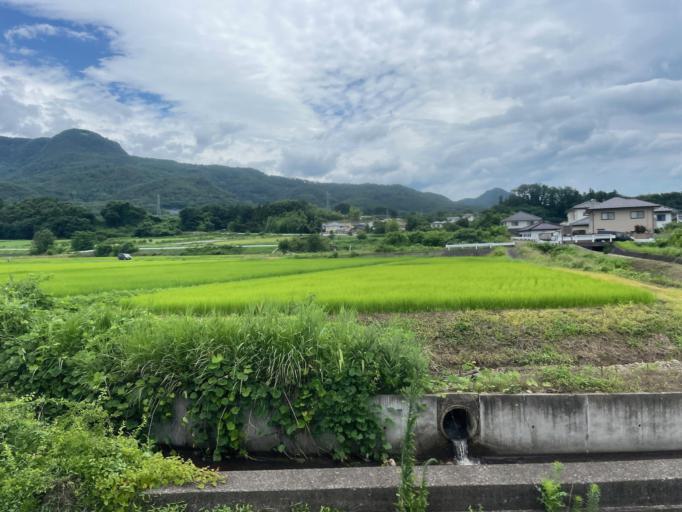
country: JP
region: Gunma
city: Numata
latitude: 36.6664
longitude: 139.0175
